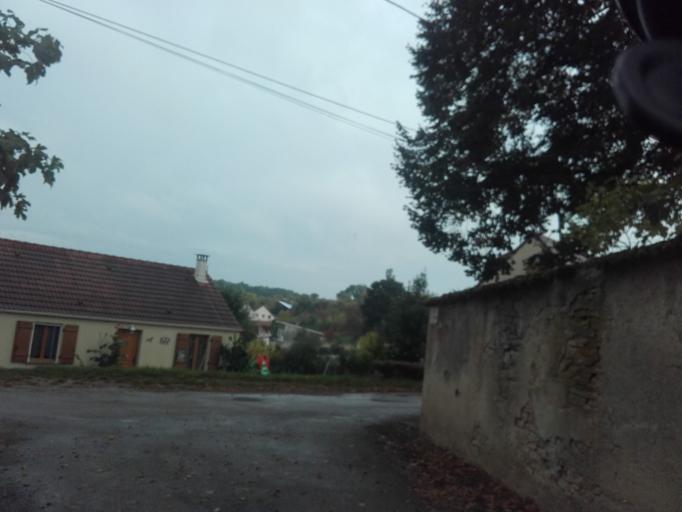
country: FR
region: Bourgogne
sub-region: Departement de la Cote-d'Or
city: Savigny-les-Beaune
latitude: 47.0505
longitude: 4.7717
